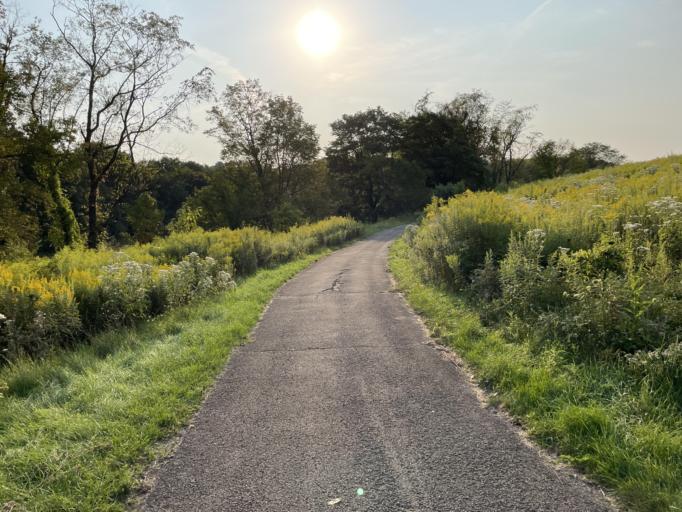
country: US
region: Pennsylvania
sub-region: Allegheny County
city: Churchill
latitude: 40.4496
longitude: -79.8432
